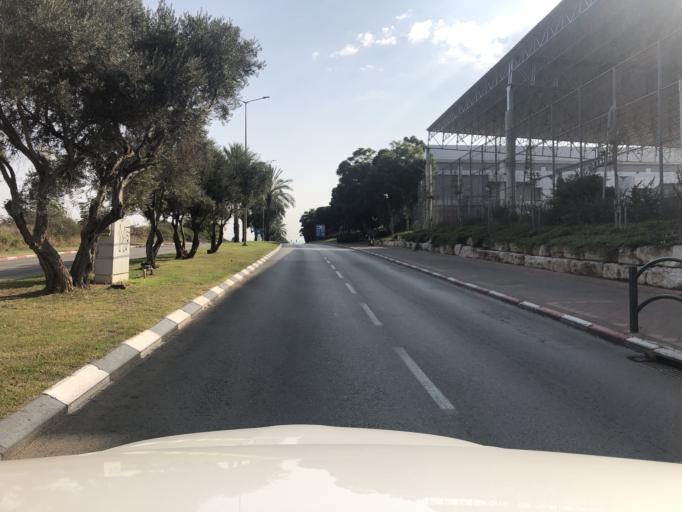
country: IL
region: Central District
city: Kfar Saba
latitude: 32.1857
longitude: 34.9097
